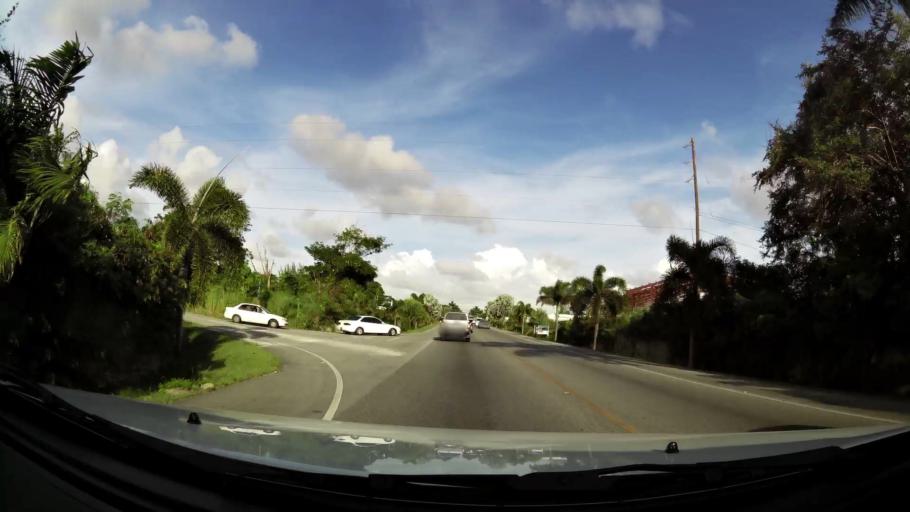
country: BB
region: Christ Church
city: Oistins
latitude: 13.0779
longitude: -59.5601
